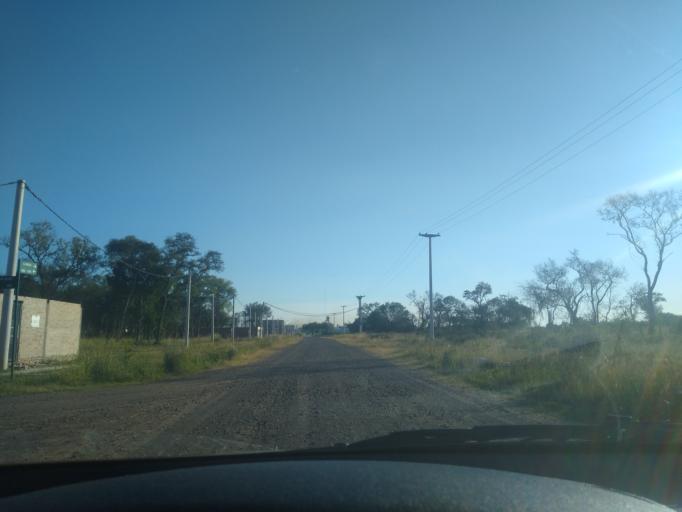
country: AR
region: Chaco
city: Resistencia
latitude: -27.4103
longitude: -58.9552
